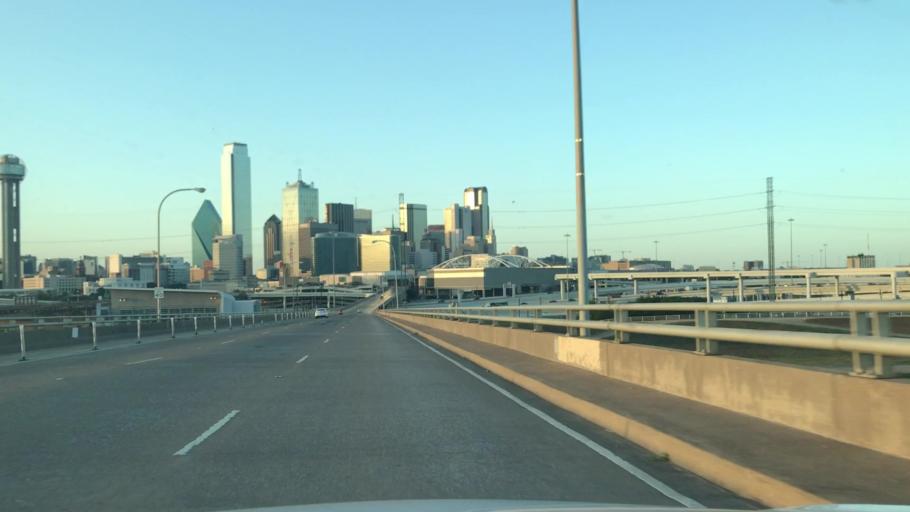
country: US
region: Texas
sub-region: Dallas County
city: Dallas
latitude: 32.7653
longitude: -96.8107
